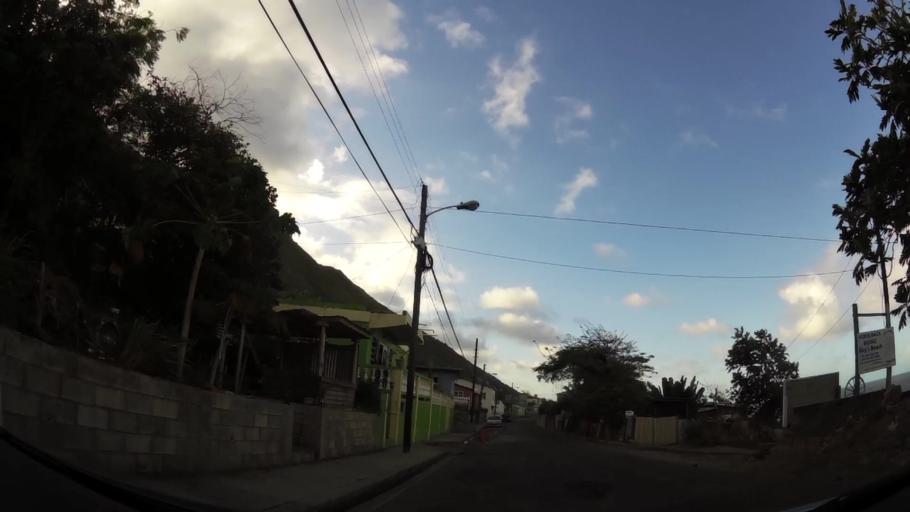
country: KN
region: Saint Mary Cayon
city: Cayon
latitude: 17.3403
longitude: -62.7122
